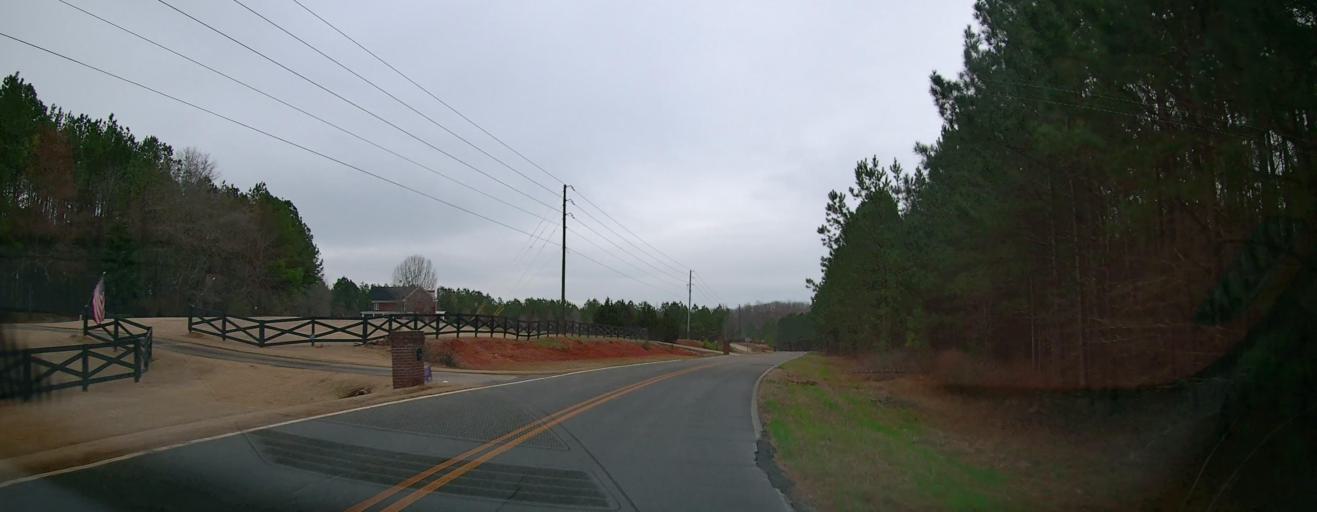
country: US
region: Georgia
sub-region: Monroe County
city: Forsyth
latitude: 33.0023
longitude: -83.8305
